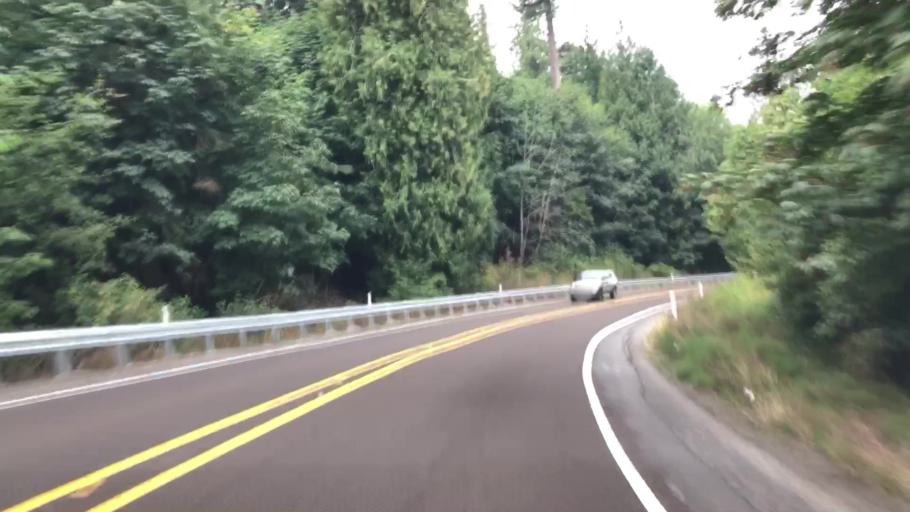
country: US
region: Washington
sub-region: Kitsap County
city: Navy Yard City
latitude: 47.5269
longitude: -122.7281
